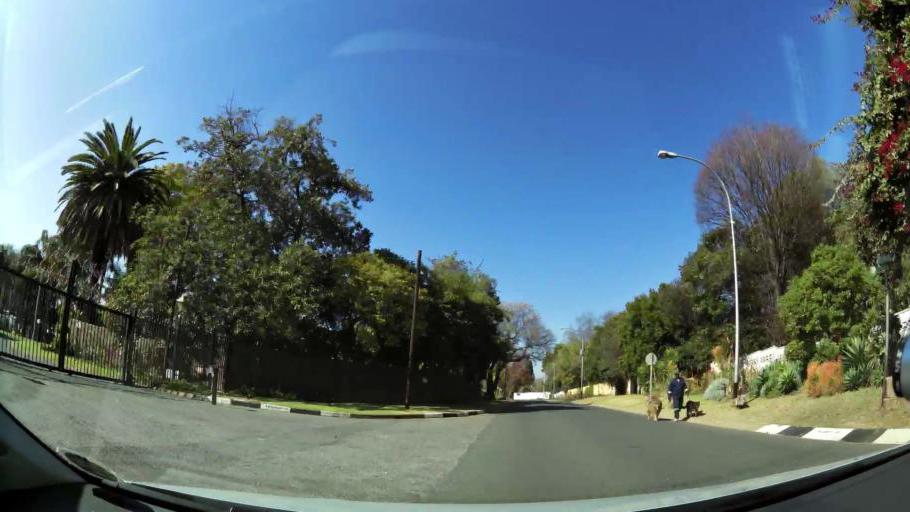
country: ZA
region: Gauteng
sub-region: City of Johannesburg Metropolitan Municipality
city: Modderfontein
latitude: -26.1354
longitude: 28.1128
